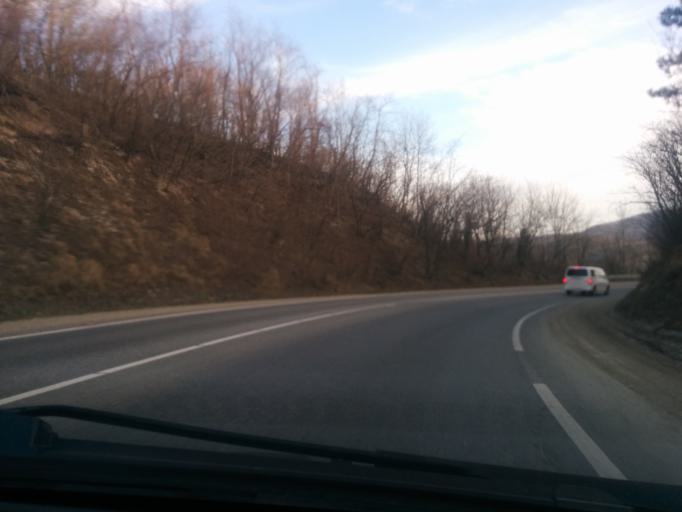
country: RU
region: Krasnodarskiy
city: Novomikhaylovskiy
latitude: 44.2467
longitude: 38.8907
